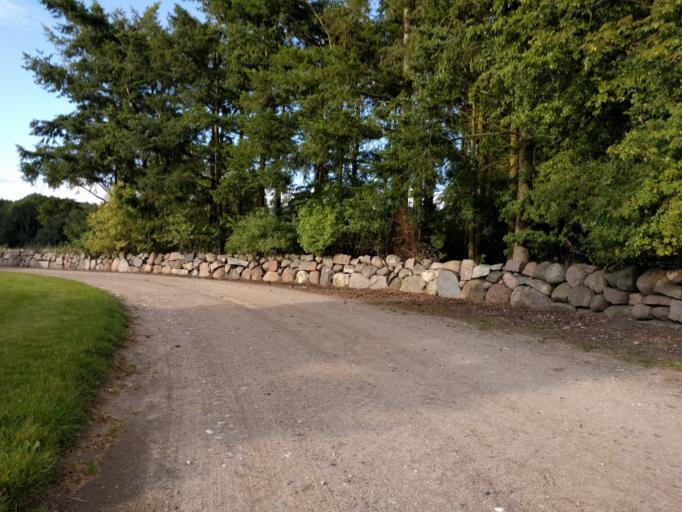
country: DK
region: South Denmark
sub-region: Kerteminde Kommune
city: Langeskov
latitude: 55.3920
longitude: 10.5463
